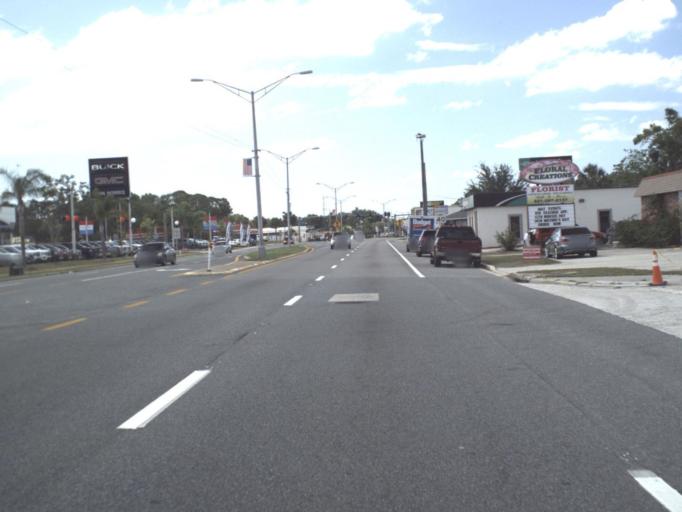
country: US
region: Florida
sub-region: Brevard County
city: Titusville
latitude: 28.5986
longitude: -80.8066
